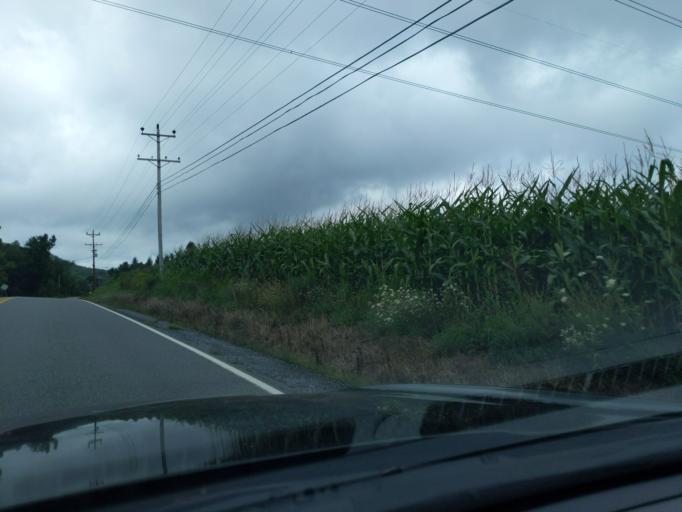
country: US
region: Pennsylvania
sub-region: Blair County
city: Claysburg
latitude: 40.3361
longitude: -78.5597
